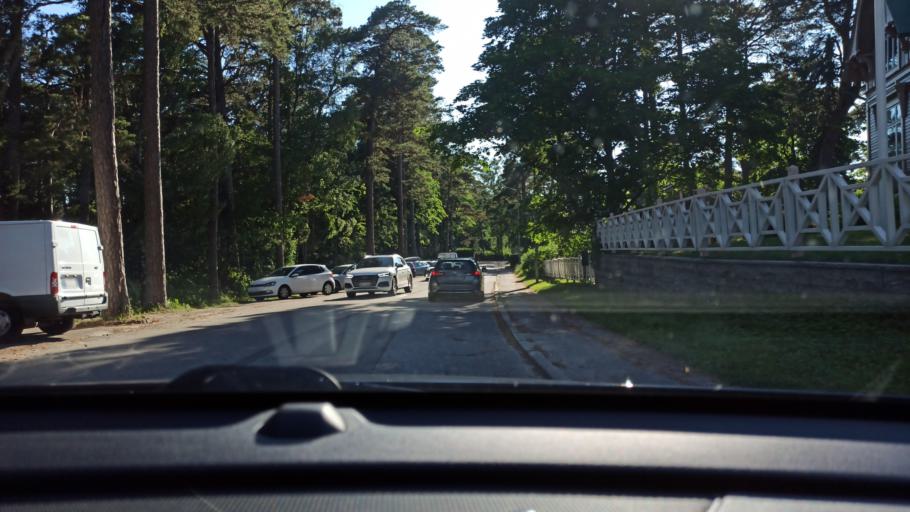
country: FI
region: Uusimaa
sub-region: Raaseporin
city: Hanko
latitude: 59.8258
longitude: 22.9837
